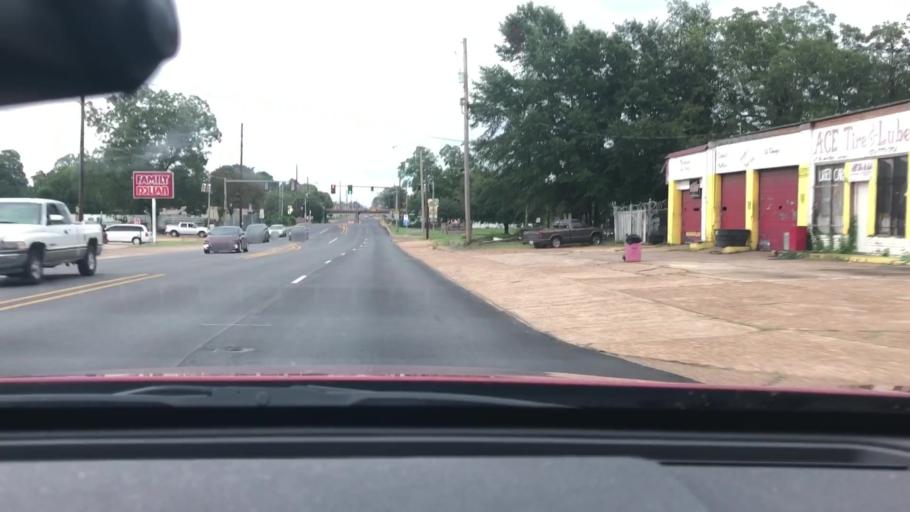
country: US
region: Arkansas
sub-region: Miller County
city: Texarkana
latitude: 33.4308
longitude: -94.0309
